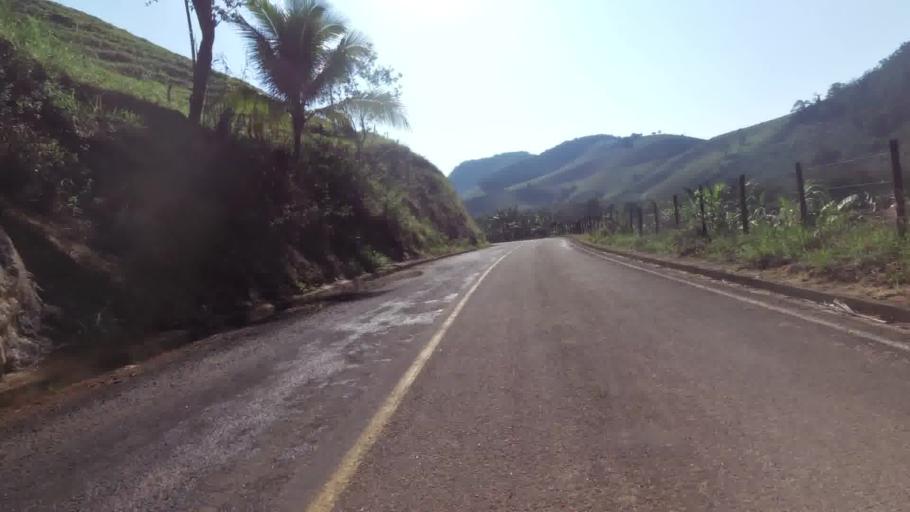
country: BR
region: Espirito Santo
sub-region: Alfredo Chaves
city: Alfredo Chaves
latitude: -20.6864
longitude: -40.7763
